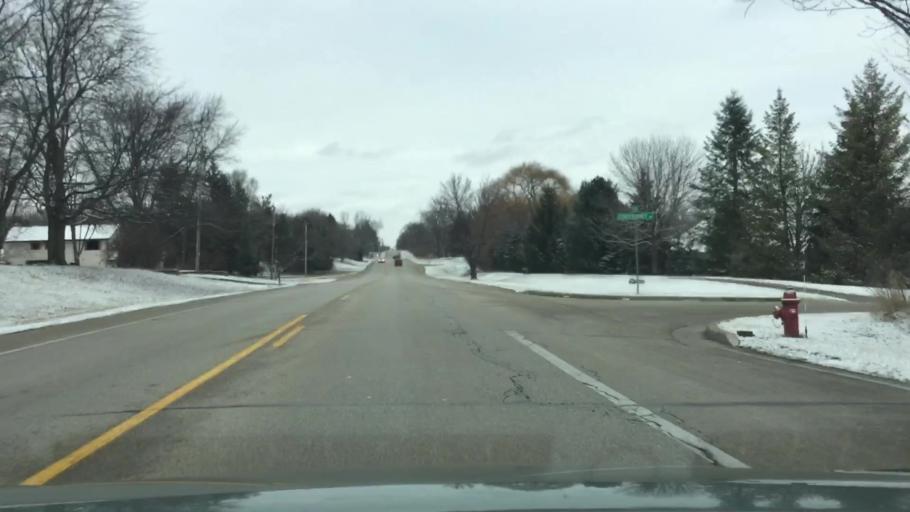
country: US
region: Wisconsin
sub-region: Waukesha County
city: Brookfield
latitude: 43.0931
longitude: -88.1058
